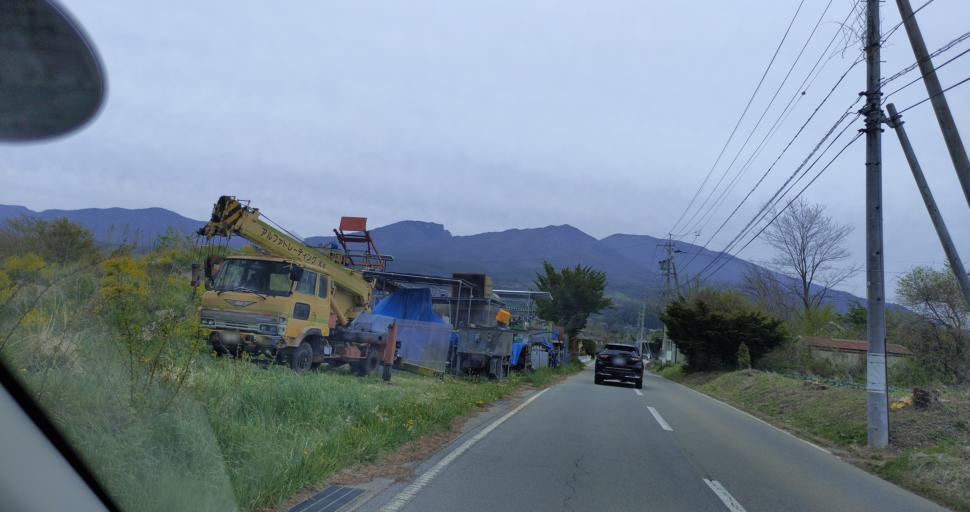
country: JP
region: Nagano
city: Komoro
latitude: 36.3302
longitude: 138.4889
